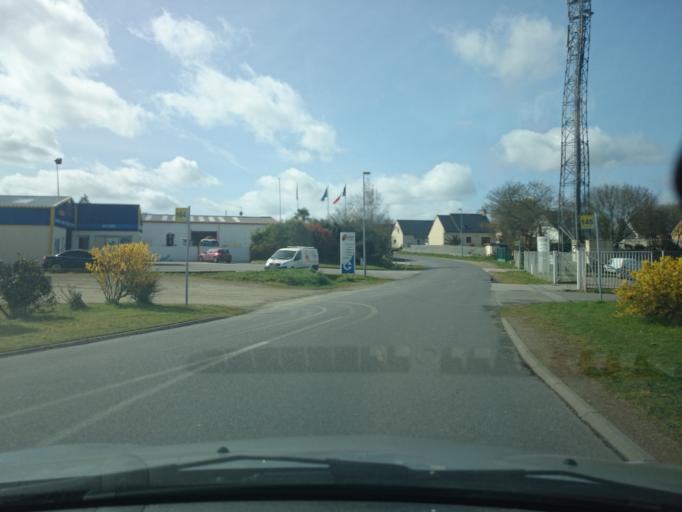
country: FR
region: Brittany
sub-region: Departement du Finistere
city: Gouesnou
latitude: 48.4576
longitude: -4.4511
